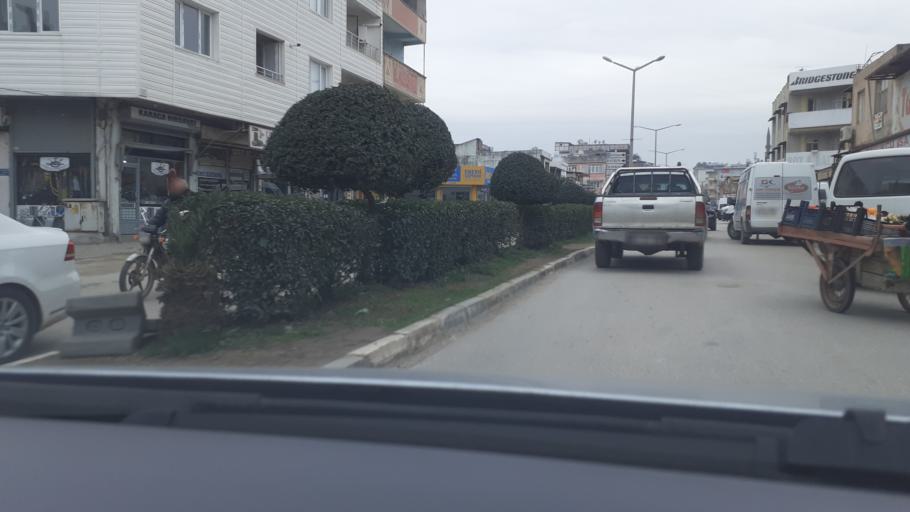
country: TR
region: Hatay
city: Kirikhan
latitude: 36.4972
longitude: 36.3609
